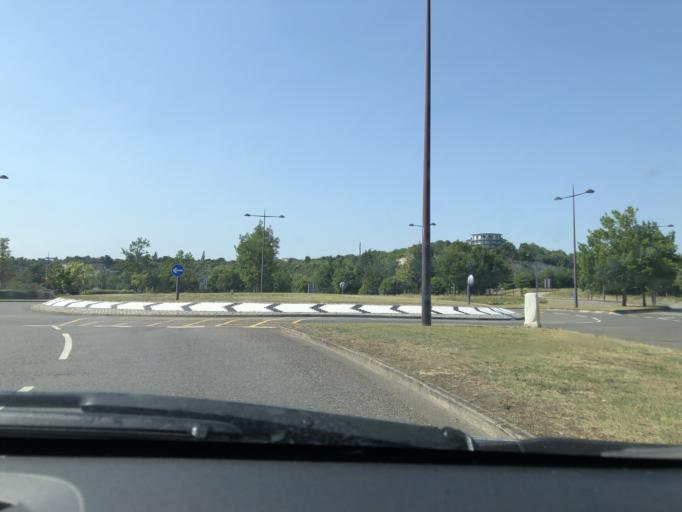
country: GB
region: England
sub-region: Kent
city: Greenhithe
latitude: 51.4385
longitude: 0.2778
